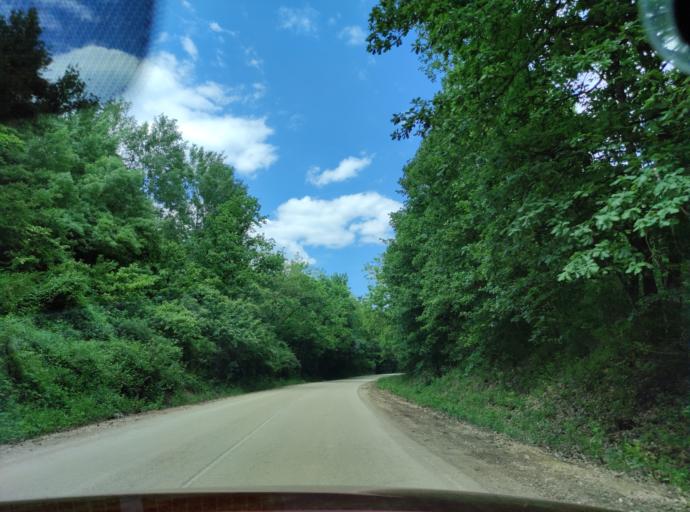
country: BG
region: Montana
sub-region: Obshtina Berkovitsa
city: Berkovitsa
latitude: 43.3770
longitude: 23.0761
